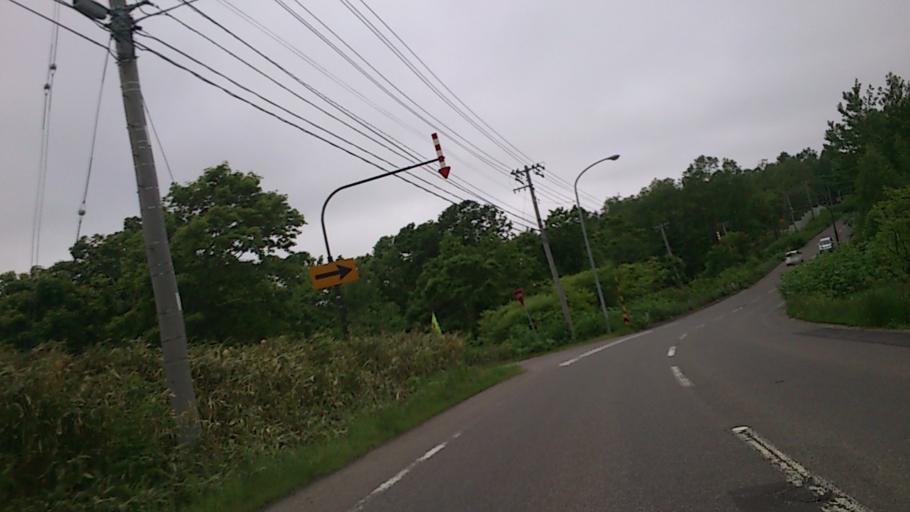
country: JP
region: Hokkaido
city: Niseko Town
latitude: 42.8396
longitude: 140.6476
